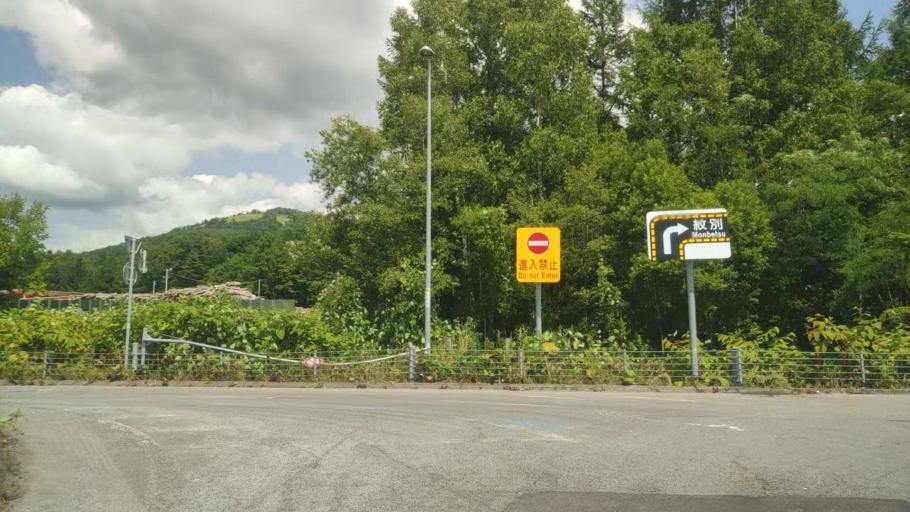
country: JP
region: Hokkaido
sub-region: Asahikawa-shi
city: Asahikawa
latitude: 43.9198
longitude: 142.4987
